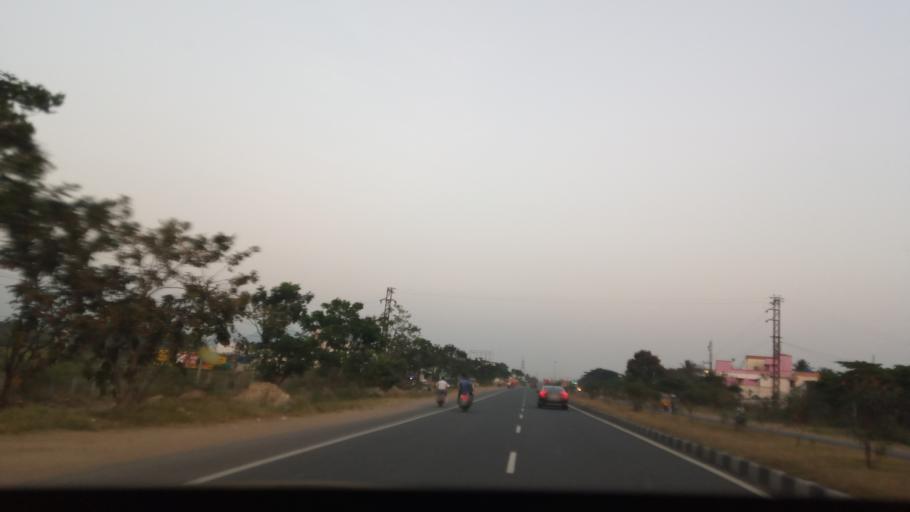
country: IN
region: Tamil Nadu
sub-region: Salem
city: Salem
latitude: 11.6659
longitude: 78.2665
